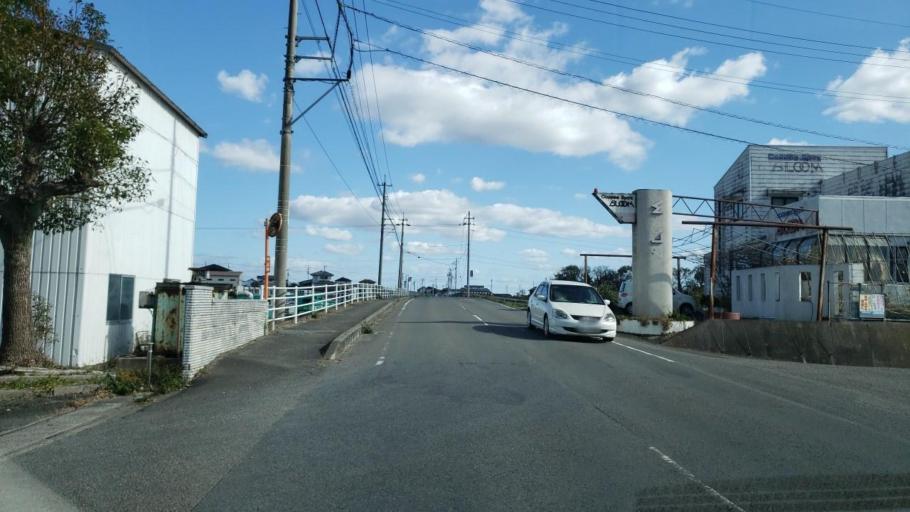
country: JP
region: Tokushima
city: Wakimachi
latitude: 34.0823
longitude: 134.2229
